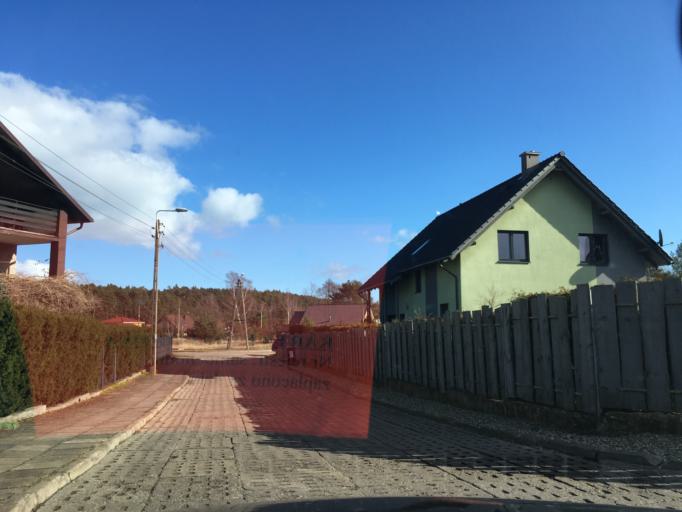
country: PL
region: Pomeranian Voivodeship
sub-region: Powiat gdanski
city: Cedry Wielkie
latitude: 54.3392
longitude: 18.8894
